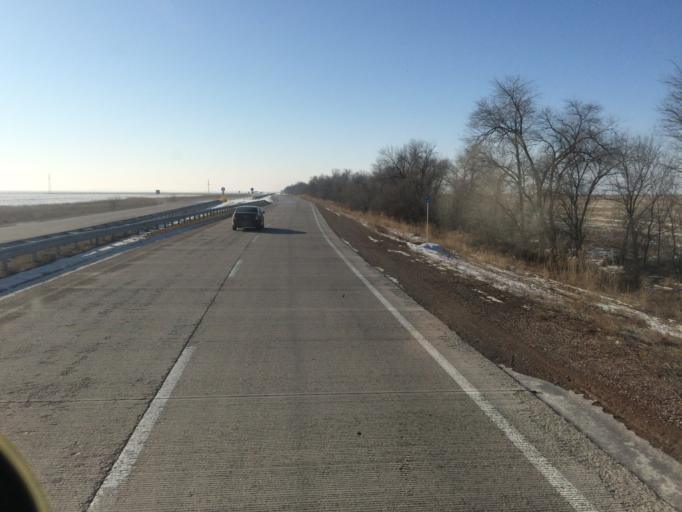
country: KG
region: Chuy
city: Belovodskoye
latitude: 43.2160
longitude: 74.1326
